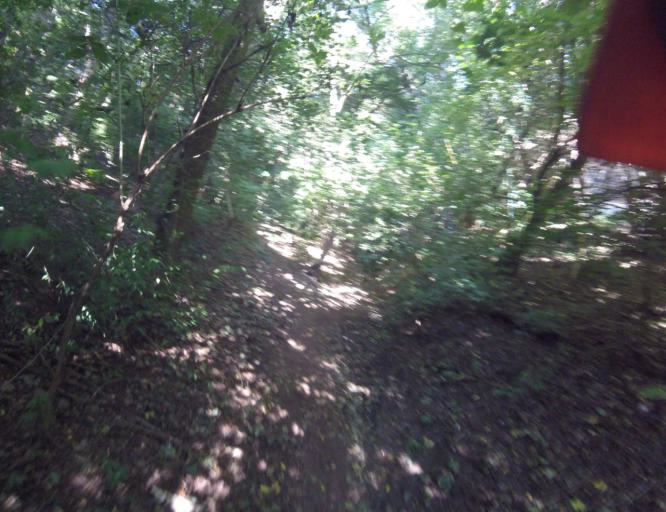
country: HU
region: Fejer
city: Gardony
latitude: 47.2488
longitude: 18.5919
